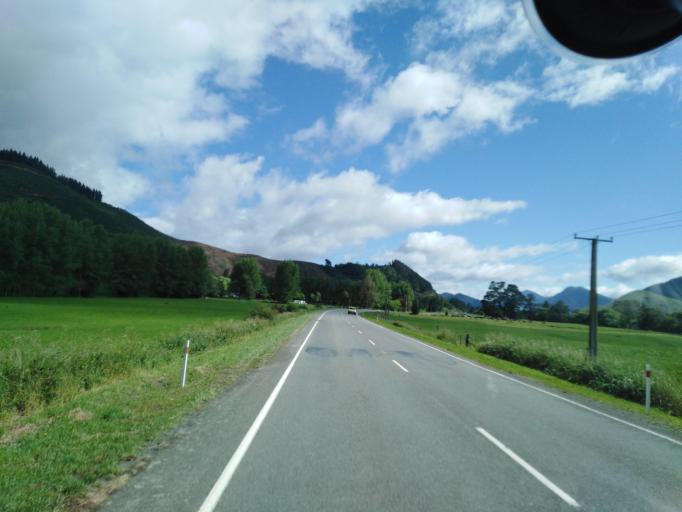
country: NZ
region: Nelson
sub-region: Nelson City
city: Nelson
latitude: -41.2693
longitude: 173.5725
